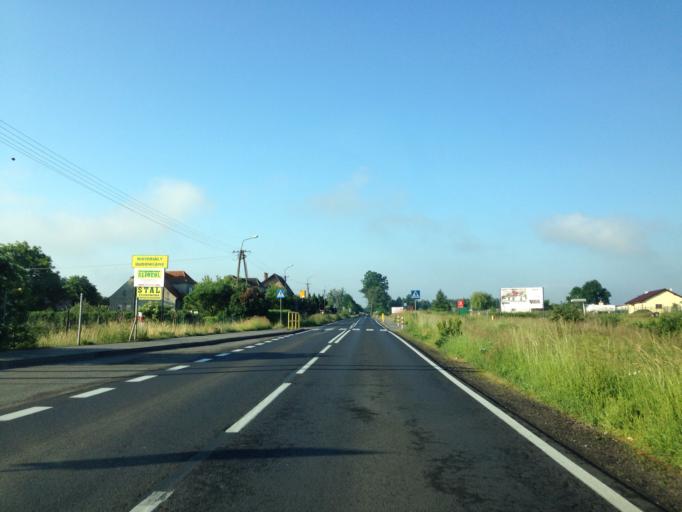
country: PL
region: Kujawsko-Pomorskie
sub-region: Grudziadz
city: Grudziadz
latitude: 53.5224
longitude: 18.8109
